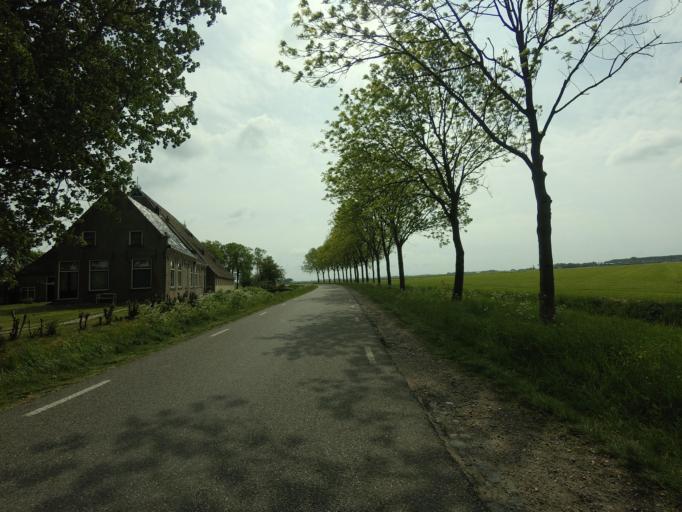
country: NL
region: Friesland
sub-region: Sudwest Fryslan
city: Bolsward
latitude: 53.1097
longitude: 5.4916
